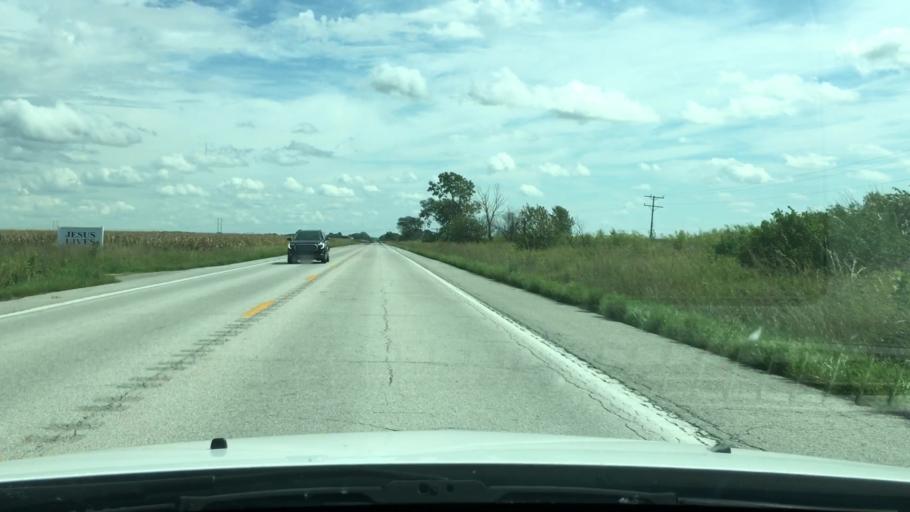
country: US
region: Missouri
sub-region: Audrain County
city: Vandalia
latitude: 39.2859
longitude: -91.5437
